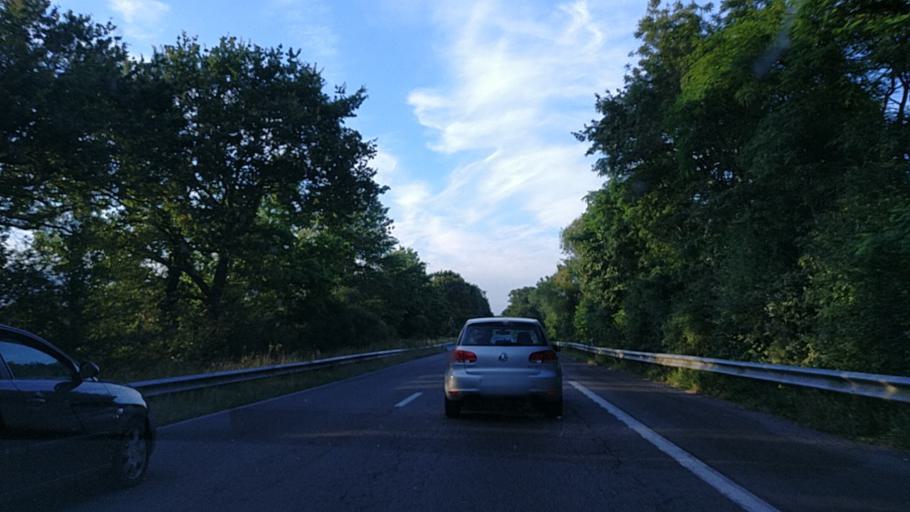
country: FR
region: Pays de la Loire
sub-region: Departement de la Loire-Atlantique
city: Heric
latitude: 47.4048
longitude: -1.6433
